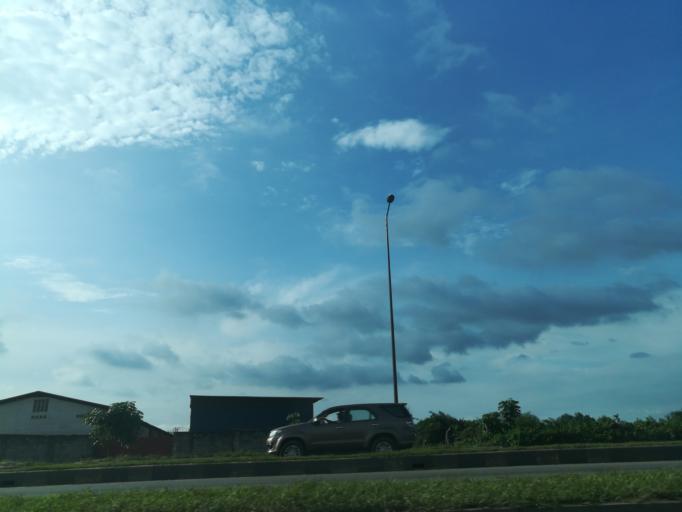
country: NG
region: Lagos
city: Ebute Ikorodu
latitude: 6.6213
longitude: 3.4521
